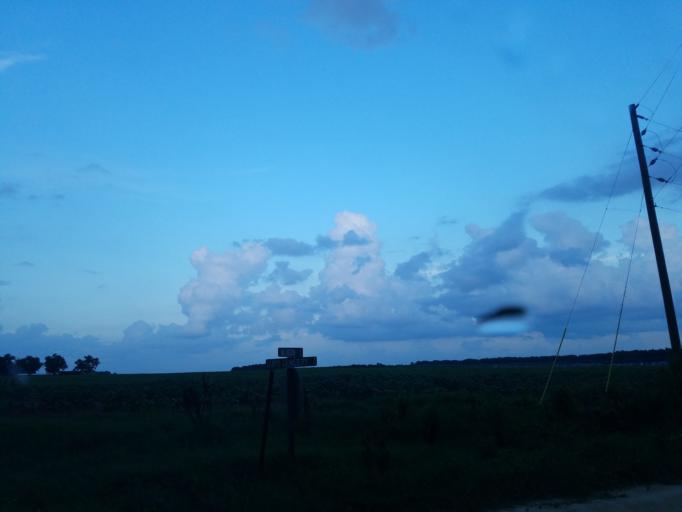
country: US
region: Georgia
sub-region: Dooly County
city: Vienna
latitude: 32.1490
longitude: -83.7275
